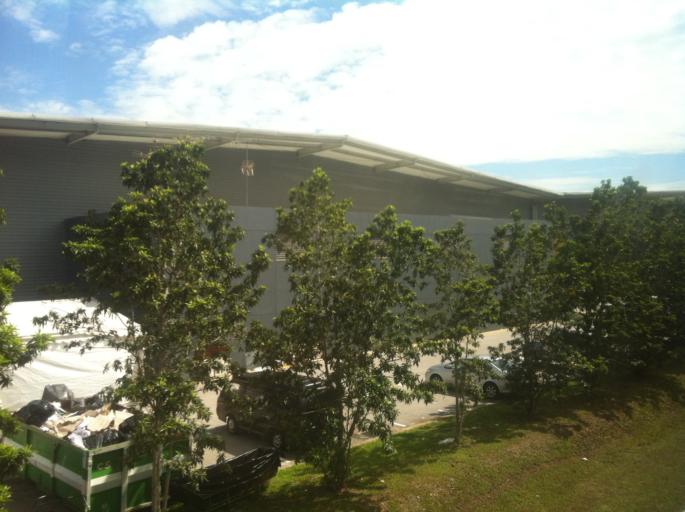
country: SG
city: Singapore
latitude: 1.3364
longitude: 103.9625
